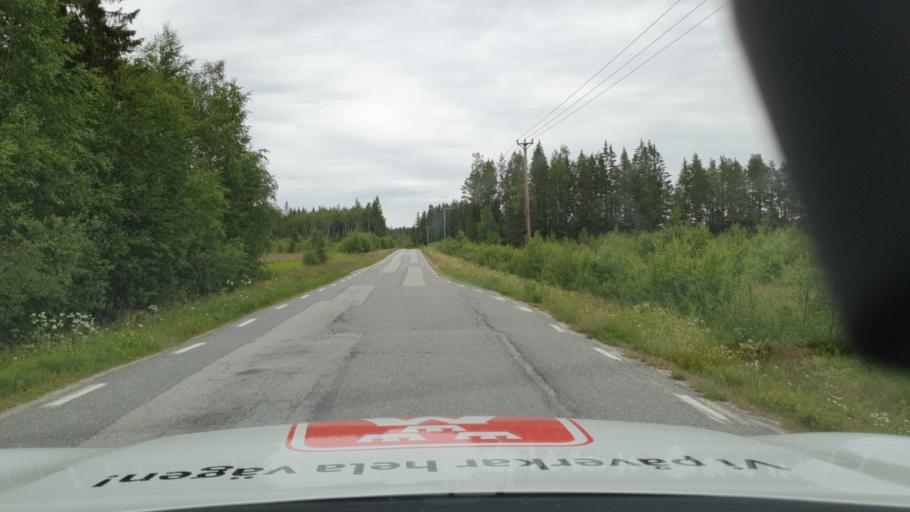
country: SE
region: Vaesterbotten
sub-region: Nordmalings Kommun
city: Nordmaling
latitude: 63.5062
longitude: 19.4182
